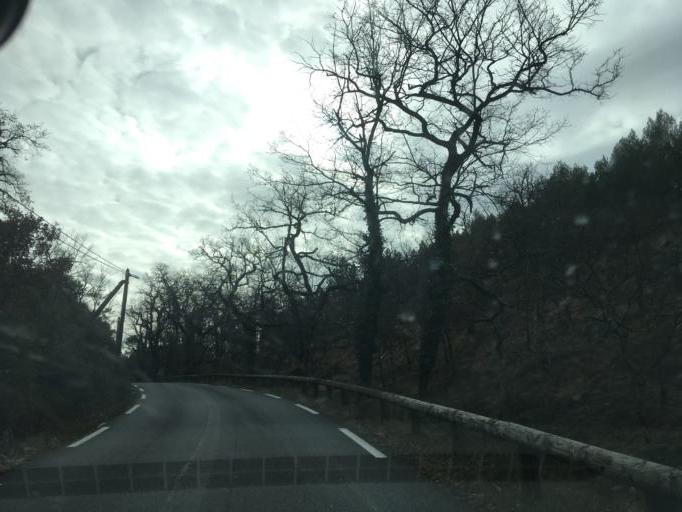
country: FR
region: Provence-Alpes-Cote d'Azur
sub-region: Departement du Var
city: Bras
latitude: 43.4554
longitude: 5.9704
